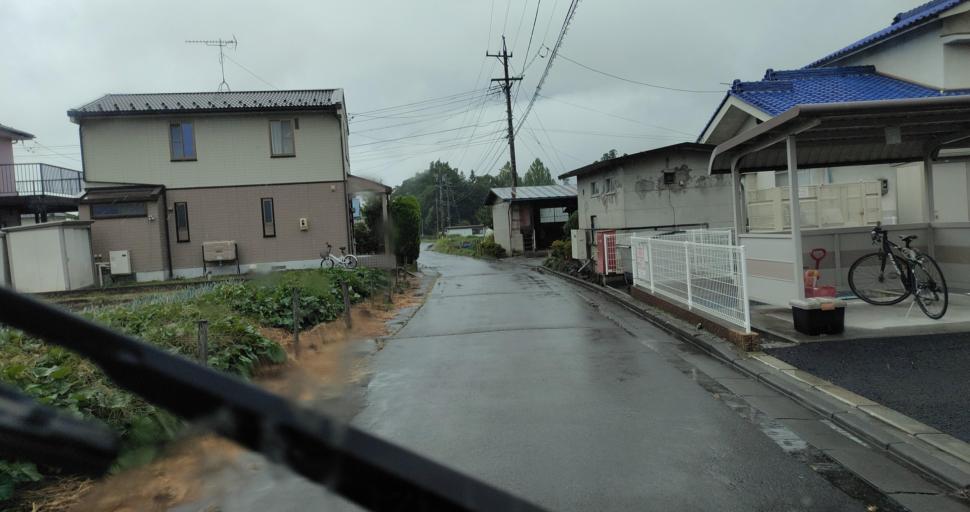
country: JP
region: Nagano
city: Saku
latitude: 36.2741
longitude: 138.4892
